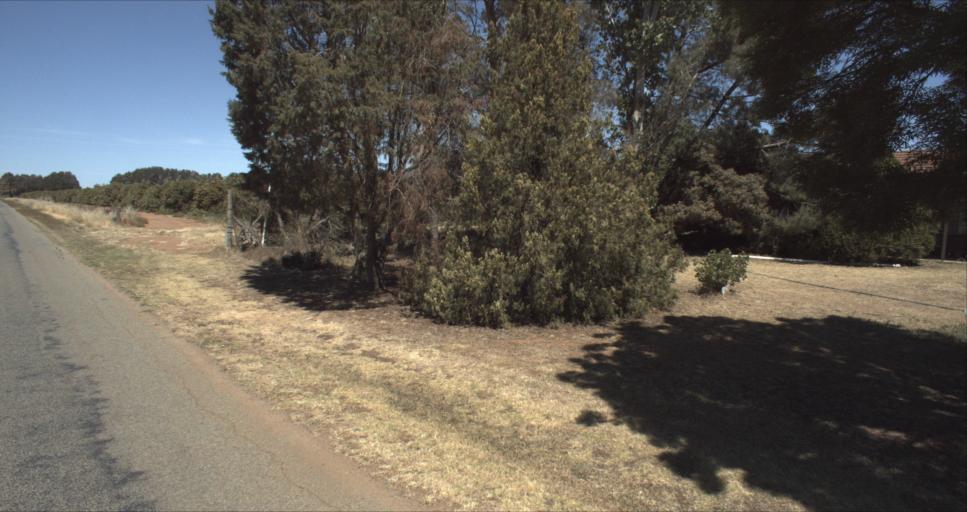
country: AU
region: New South Wales
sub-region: Leeton
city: Leeton
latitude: -34.5435
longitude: 146.3658
